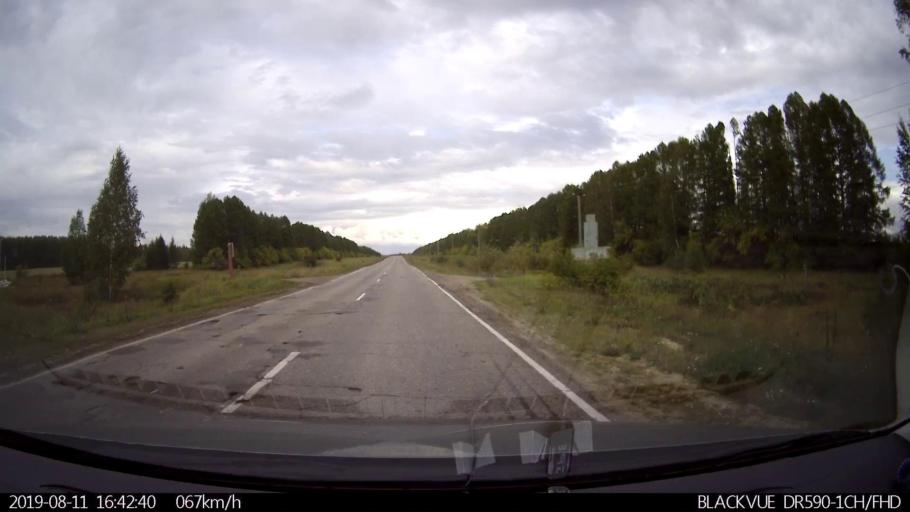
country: RU
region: Ulyanovsk
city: Mayna
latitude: 54.1622
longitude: 47.6643
